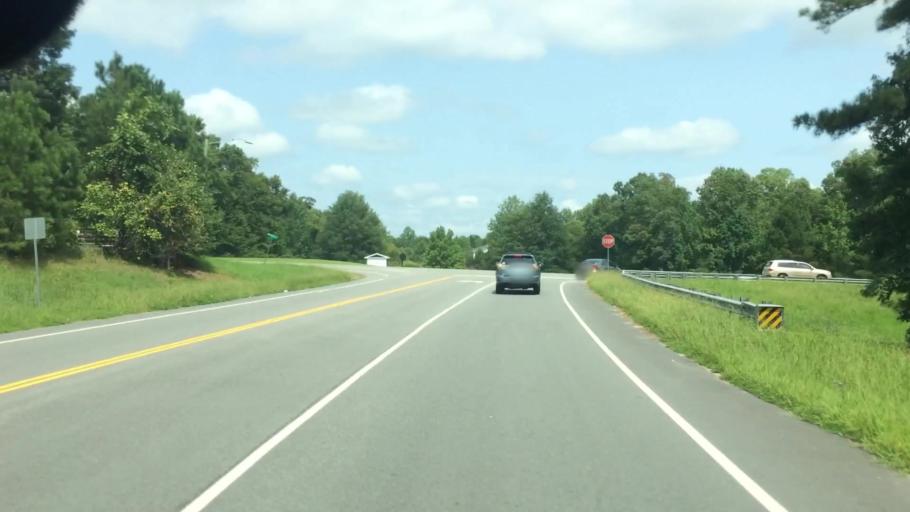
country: US
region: Virginia
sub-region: James City County
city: Williamsburg
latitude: 37.2625
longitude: -76.7886
